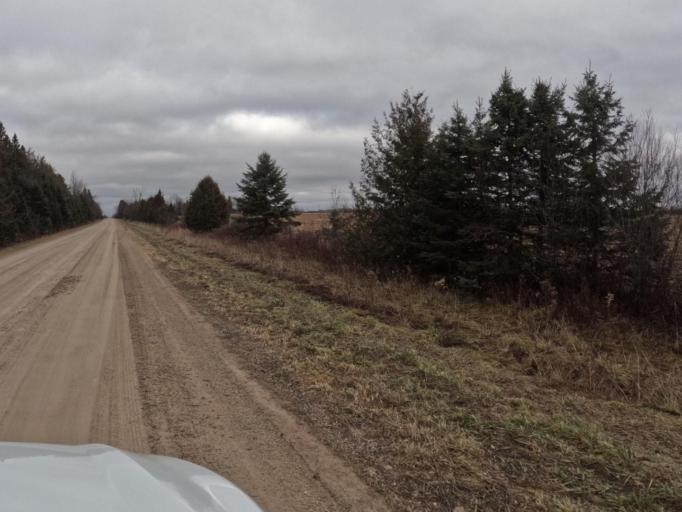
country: CA
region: Ontario
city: Shelburne
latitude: 43.9589
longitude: -80.3987
